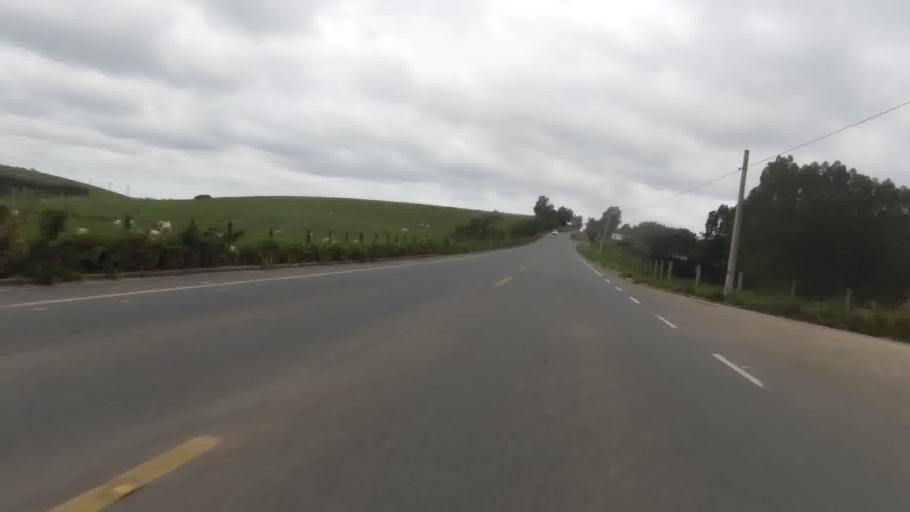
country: BR
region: Espirito Santo
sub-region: Iconha
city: Iconha
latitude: -20.7737
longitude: -40.7605
